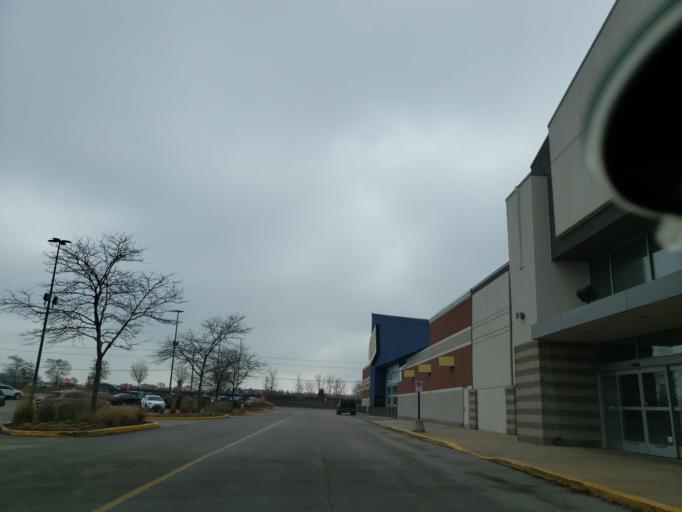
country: US
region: Illinois
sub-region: Cook County
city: Orland Hills
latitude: 41.6024
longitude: -87.8565
